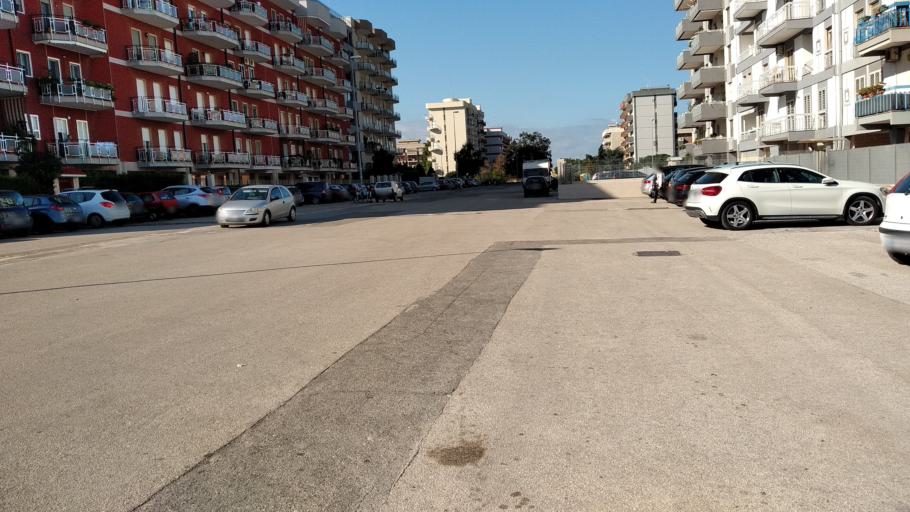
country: IT
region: Apulia
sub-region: Provincia di Bari
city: Triggiano
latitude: 41.1056
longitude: 16.9105
